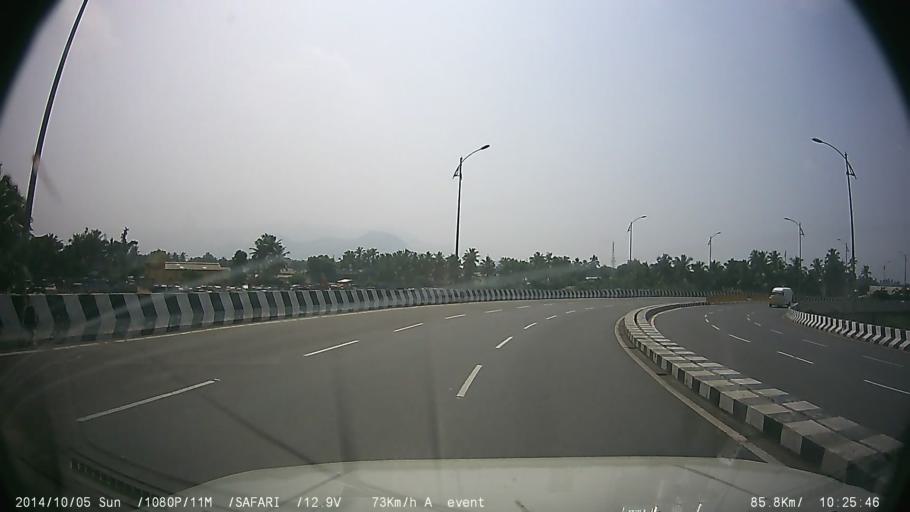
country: IN
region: Tamil Nadu
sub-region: Salem
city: Salem
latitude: 11.6421
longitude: 78.1211
